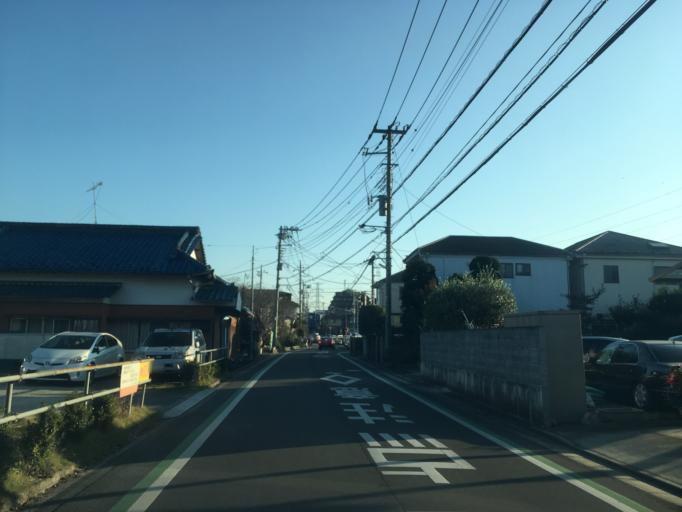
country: JP
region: Saitama
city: Tokorozawa
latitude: 35.8108
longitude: 139.4389
